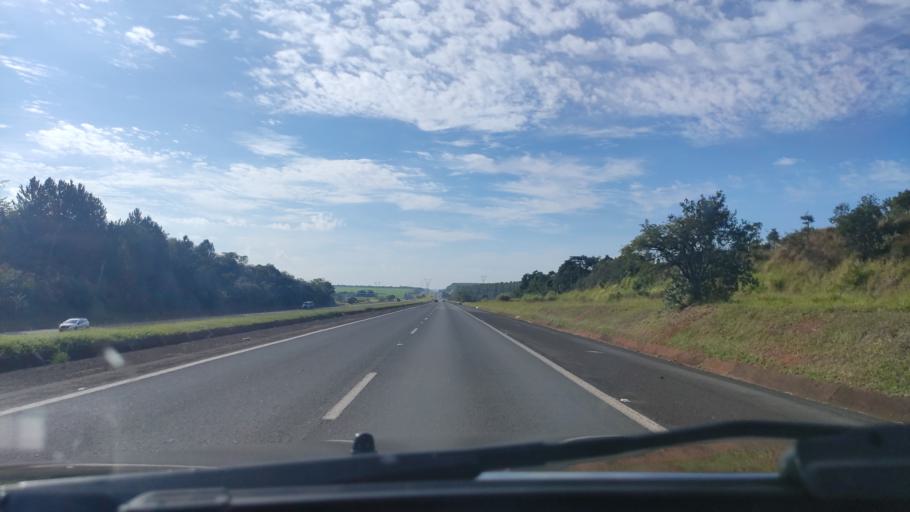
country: BR
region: Sao Paulo
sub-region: Itatinga
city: Itatinga
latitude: -23.0070
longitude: -48.7152
